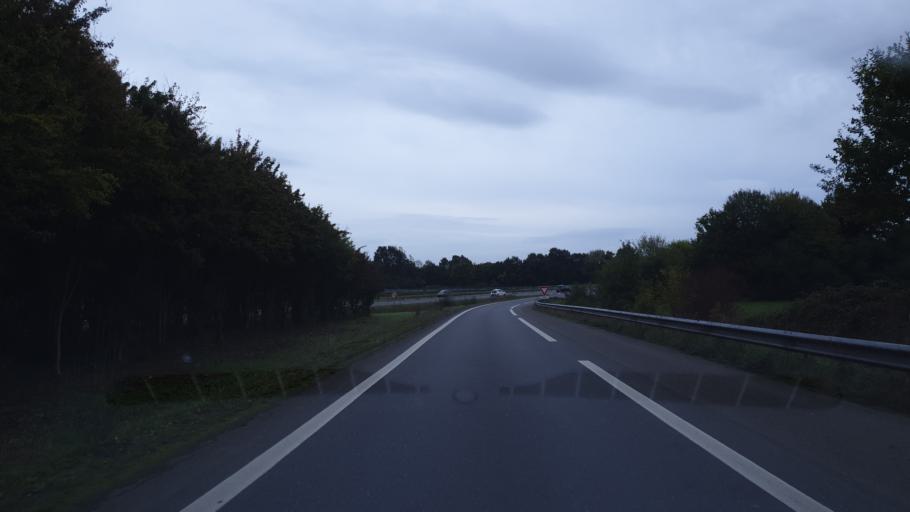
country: FR
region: Brittany
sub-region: Departement d'Ille-et-Vilaine
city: Chatillon-sur-Seiche
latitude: 48.0393
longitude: -1.6876
